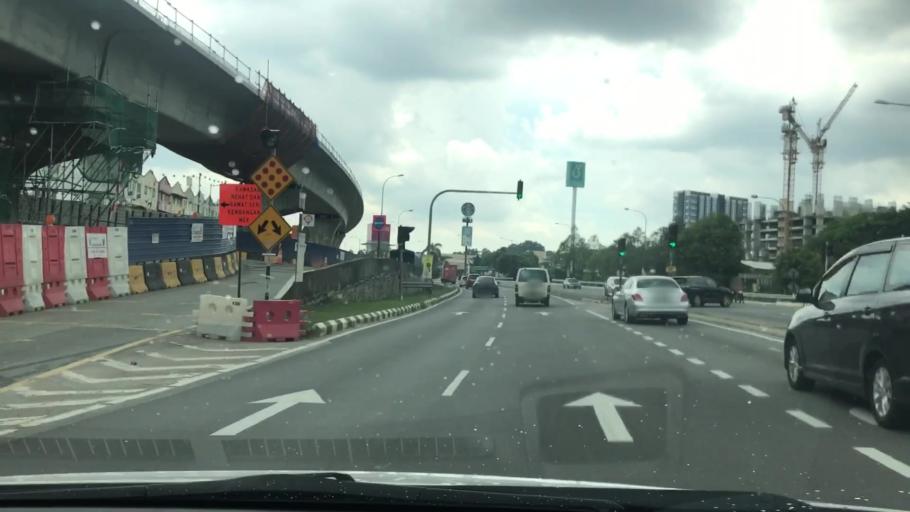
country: MY
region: Putrajaya
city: Putrajaya
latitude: 2.9954
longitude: 101.6785
